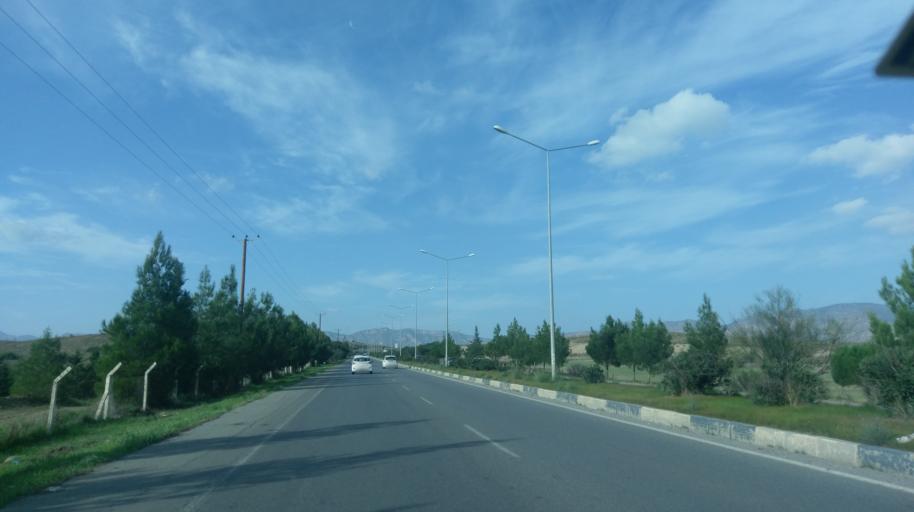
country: CY
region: Lefkosia
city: Nicosia
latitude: 35.2222
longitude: 33.3163
